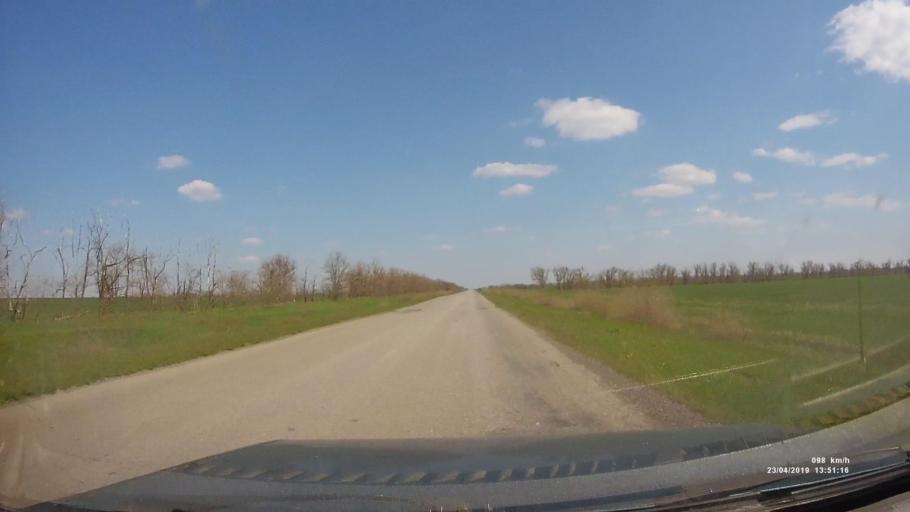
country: RU
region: Kalmykiya
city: Yashalta
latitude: 46.5995
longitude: 42.9304
